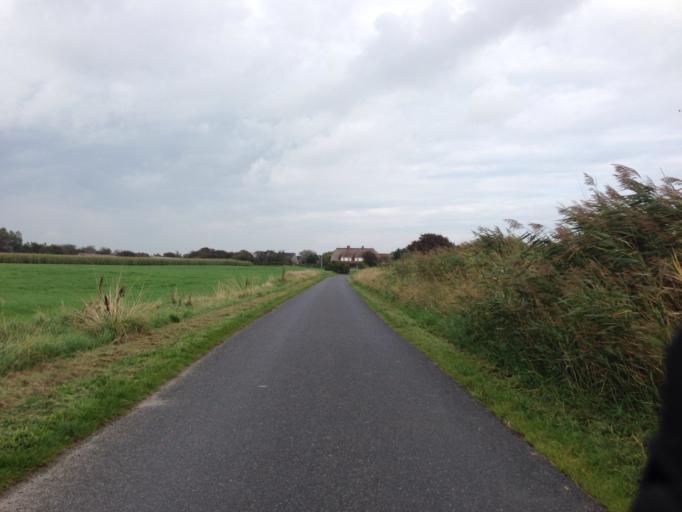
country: DE
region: Schleswig-Holstein
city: Borgsum
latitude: 54.6891
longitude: 8.4659
